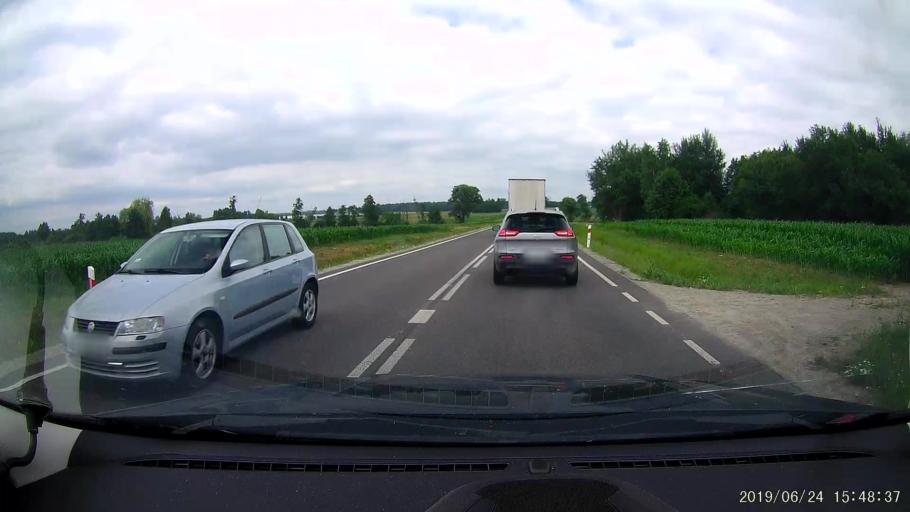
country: PL
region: Subcarpathian Voivodeship
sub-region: Powiat lubaczowski
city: Oleszyce
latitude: 50.1724
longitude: 23.0271
